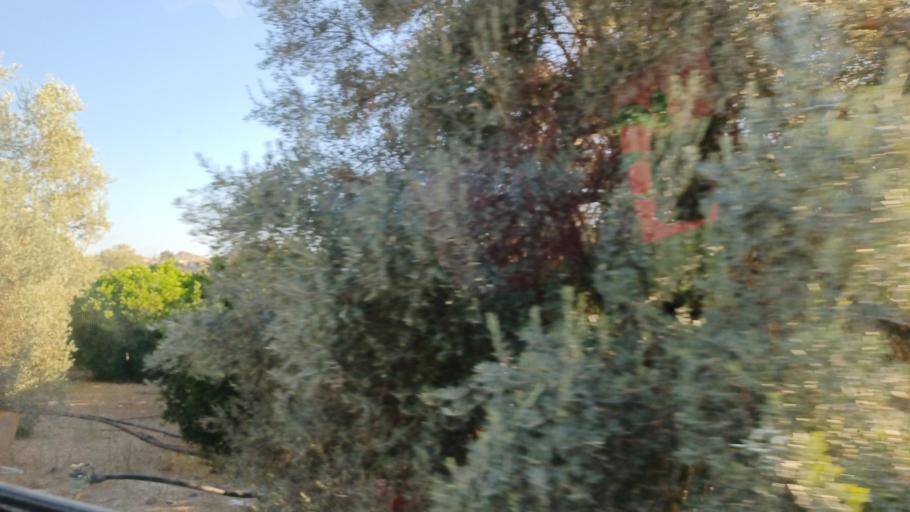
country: CY
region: Pafos
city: Polis
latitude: 34.9994
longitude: 32.4360
